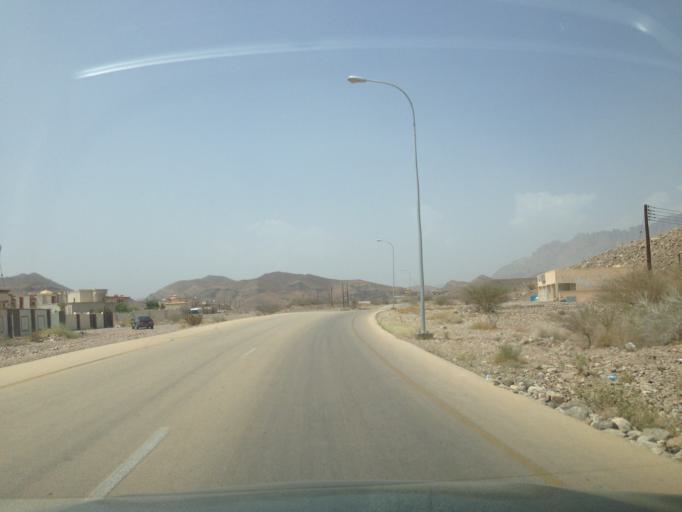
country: OM
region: Az Zahirah
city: `Ibri
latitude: 23.1779
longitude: 56.9190
